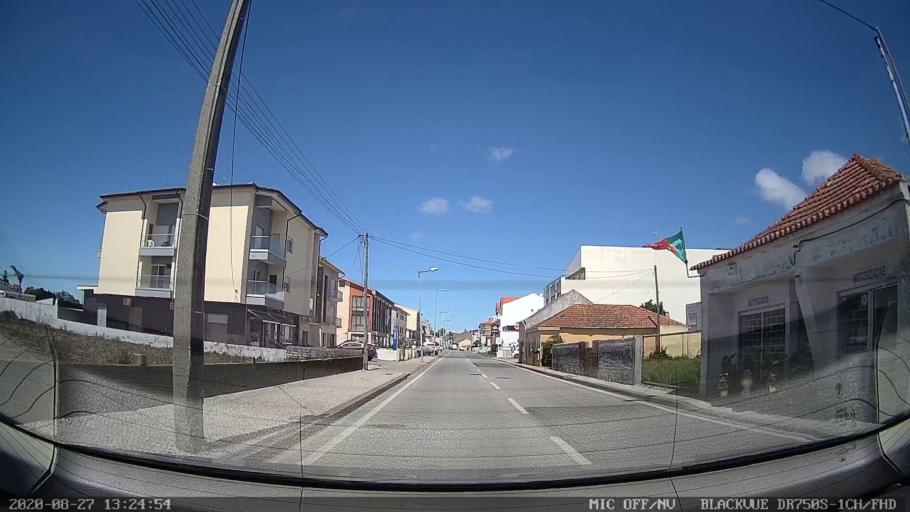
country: PT
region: Aveiro
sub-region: Vagos
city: Vagos
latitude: 40.5503
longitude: -8.6798
